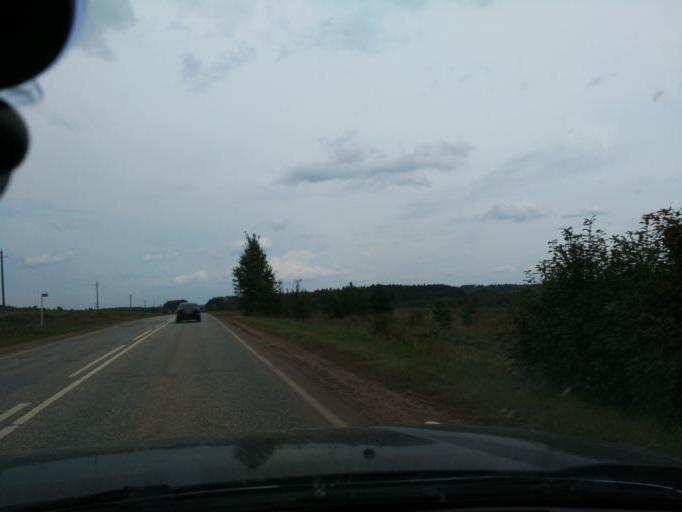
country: RU
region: Perm
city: Kuyeda
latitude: 56.4715
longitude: 55.7445
